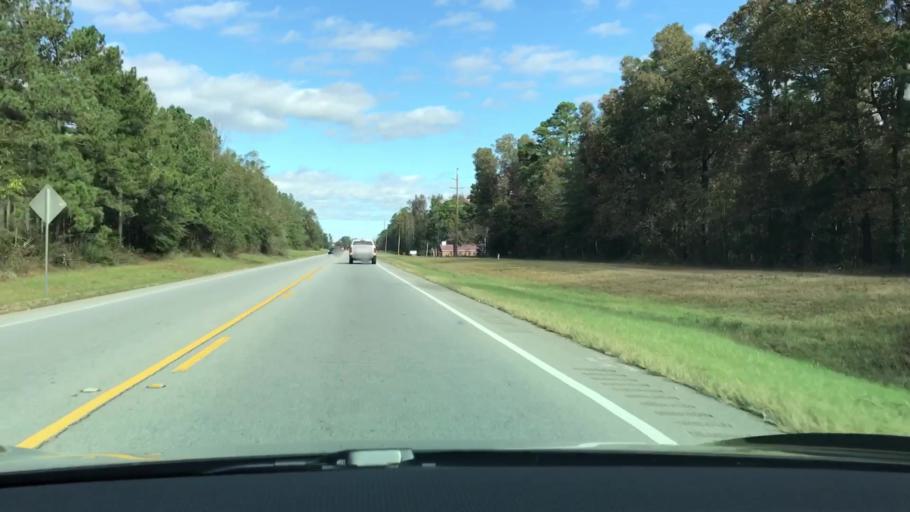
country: US
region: Georgia
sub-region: Jefferson County
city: Louisville
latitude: 33.0579
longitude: -82.4058
